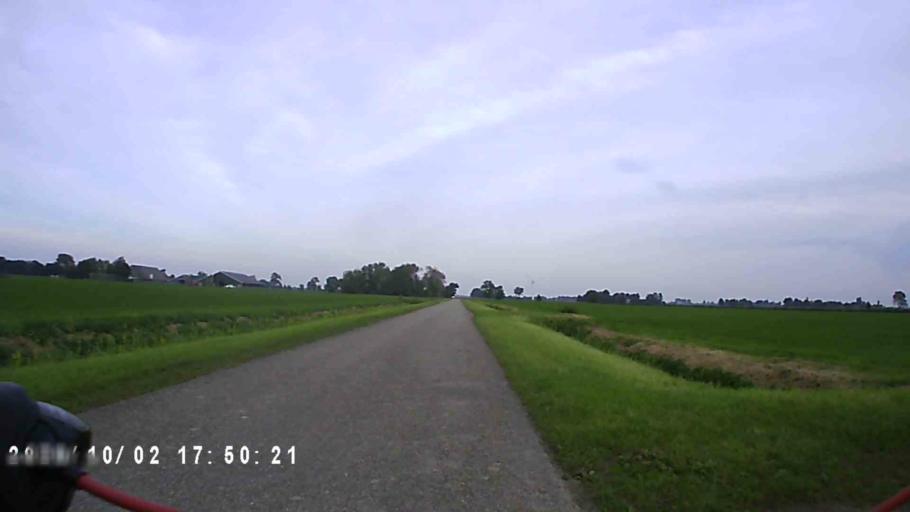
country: NL
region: Groningen
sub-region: Gemeente Zuidhorn
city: Oldehove
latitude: 53.3360
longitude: 6.4103
